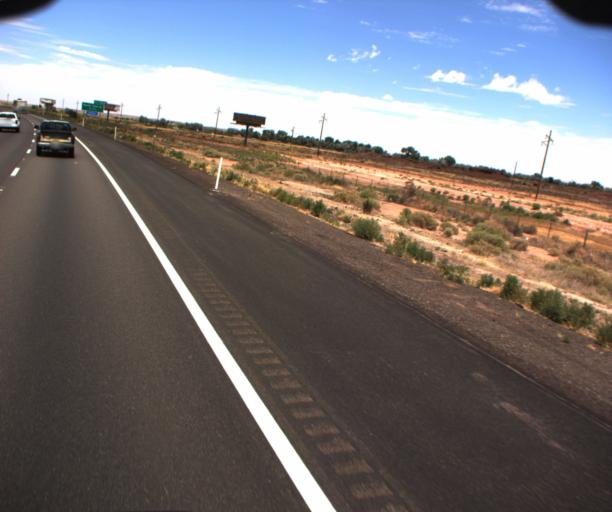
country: US
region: Arizona
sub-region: Navajo County
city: Winslow
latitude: 35.0336
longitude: -110.6861
